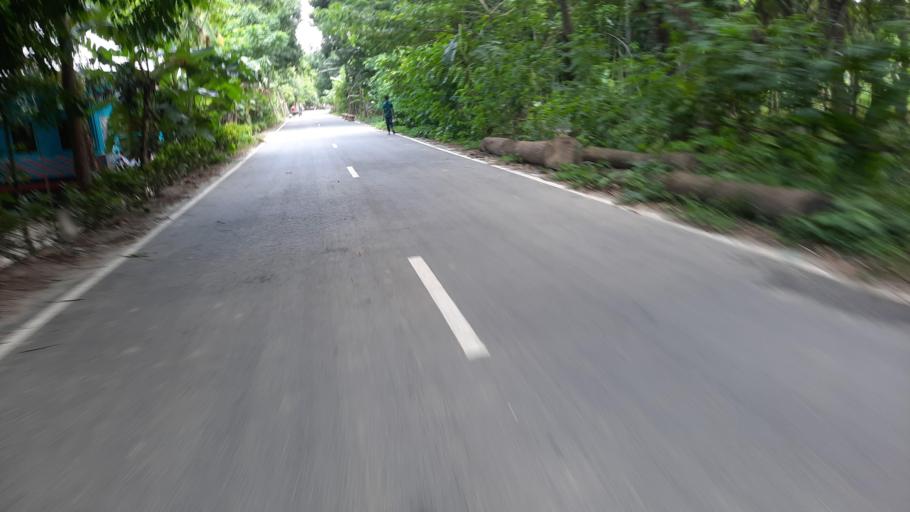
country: BD
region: Khulna
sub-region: Magura
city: Magura
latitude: 23.4494
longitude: 89.6143
